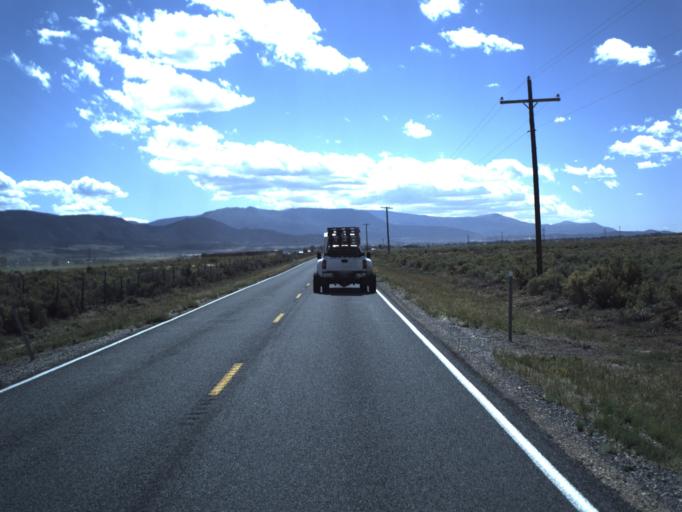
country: US
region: Utah
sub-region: Iron County
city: Enoch
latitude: 37.8160
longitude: -113.0505
